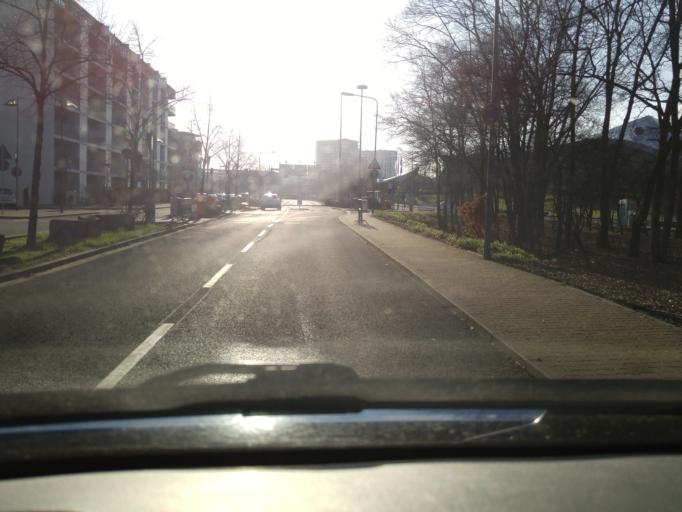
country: DE
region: Hesse
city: Niederrad
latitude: 50.1139
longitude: 8.6182
